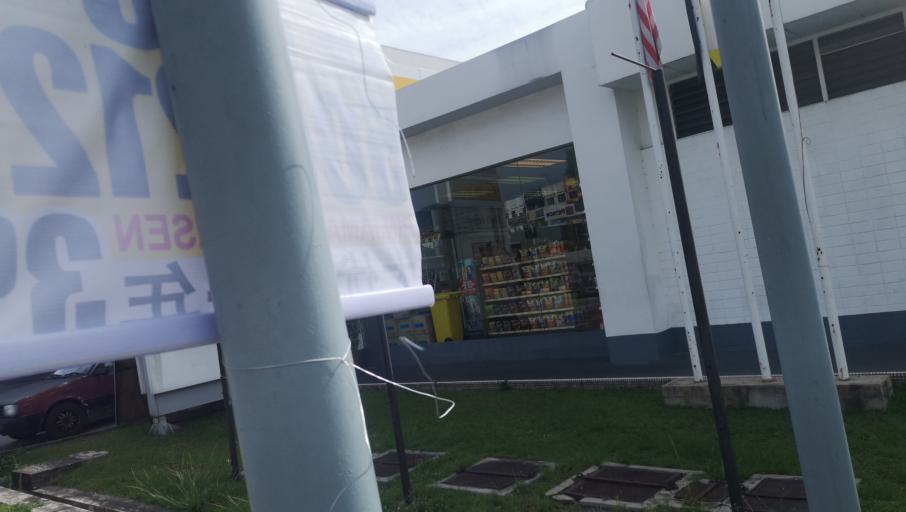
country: MY
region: Perak
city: Ipoh
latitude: 4.5927
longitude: 101.0741
